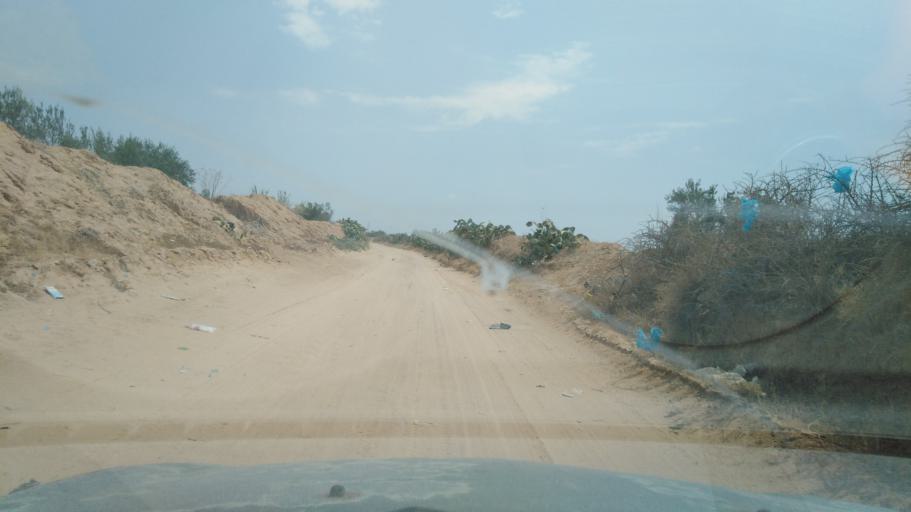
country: TN
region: Safaqis
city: Sfax
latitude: 34.7388
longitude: 10.5494
